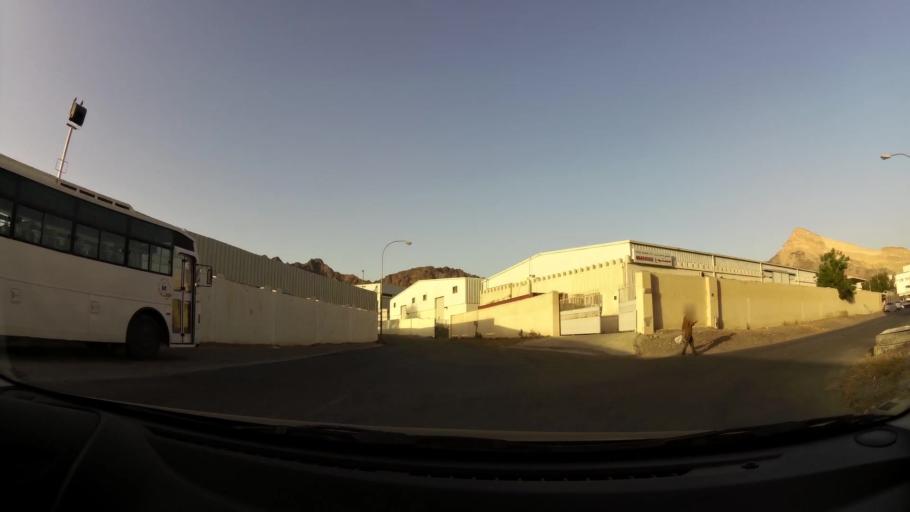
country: OM
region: Muhafazat Masqat
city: Muscat
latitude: 23.5694
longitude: 58.5749
